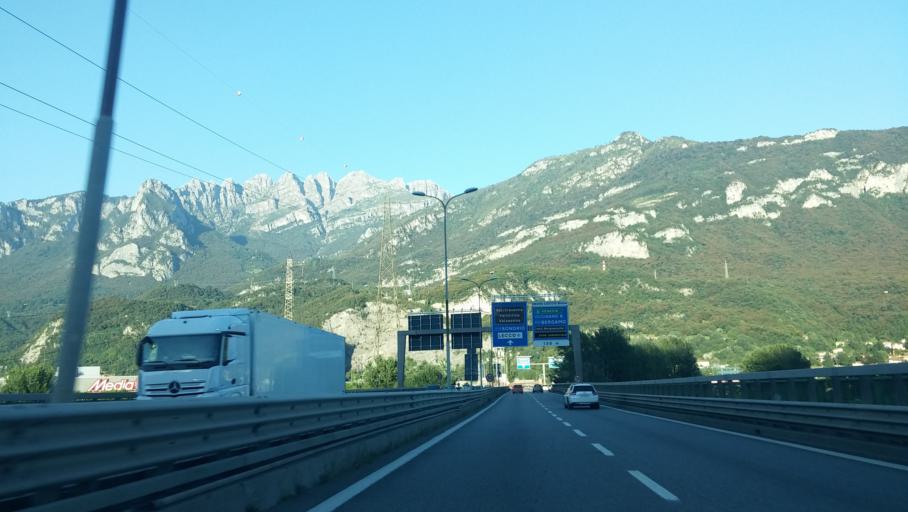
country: IT
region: Lombardy
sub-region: Provincia di Lecco
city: Pescate
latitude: 45.8388
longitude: 9.3995
